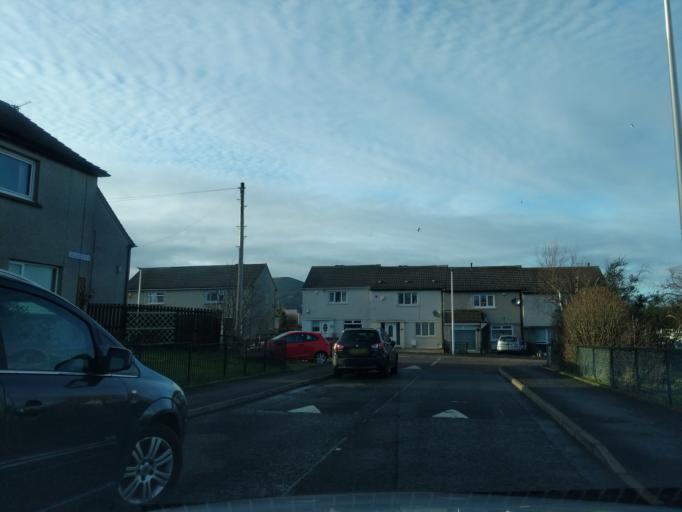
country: GB
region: Scotland
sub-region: Midlothian
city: Loanhead
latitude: 55.8790
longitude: -3.1616
